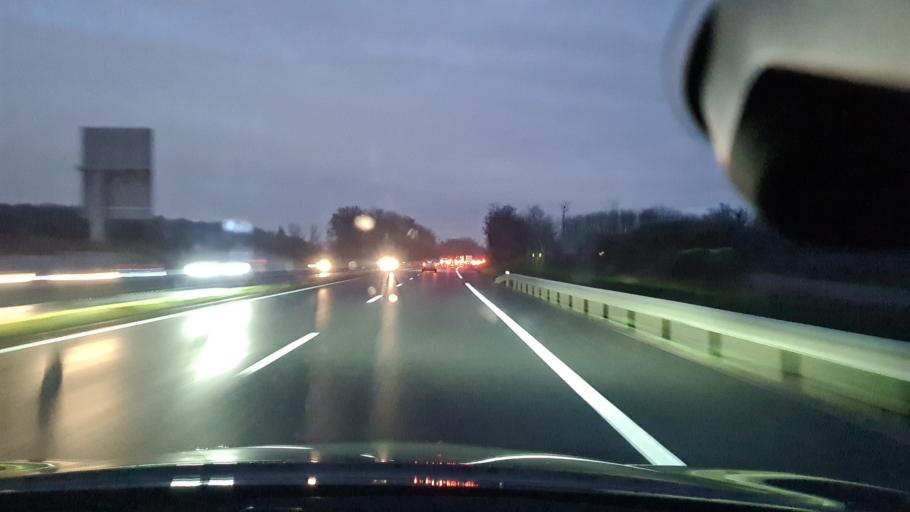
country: FR
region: Rhone-Alpes
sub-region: Departement du Rhone
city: Meyzieu
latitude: 45.7508
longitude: 5.0080
